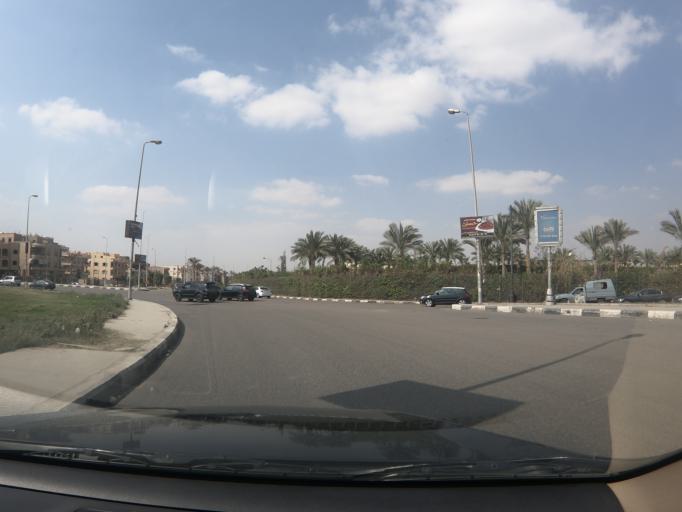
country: EG
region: Muhafazat al Qalyubiyah
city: Al Khankah
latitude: 30.0549
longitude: 31.4754
